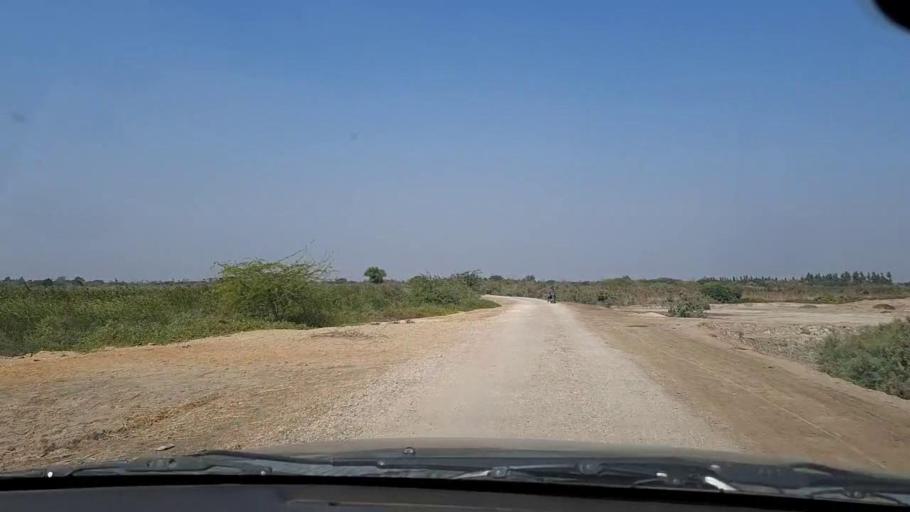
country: PK
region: Sindh
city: Chuhar Jamali
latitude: 24.4358
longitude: 67.7993
